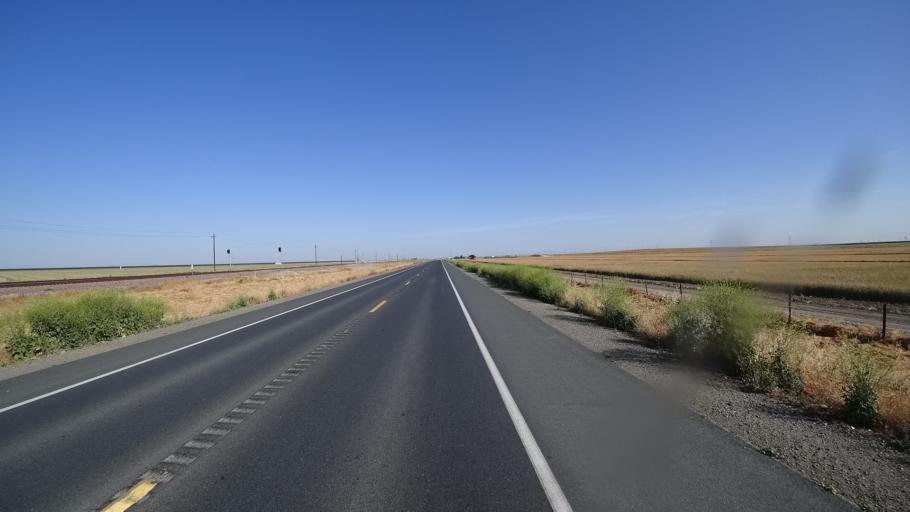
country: US
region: California
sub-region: Kings County
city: Corcoran
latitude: 36.1253
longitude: -119.5760
